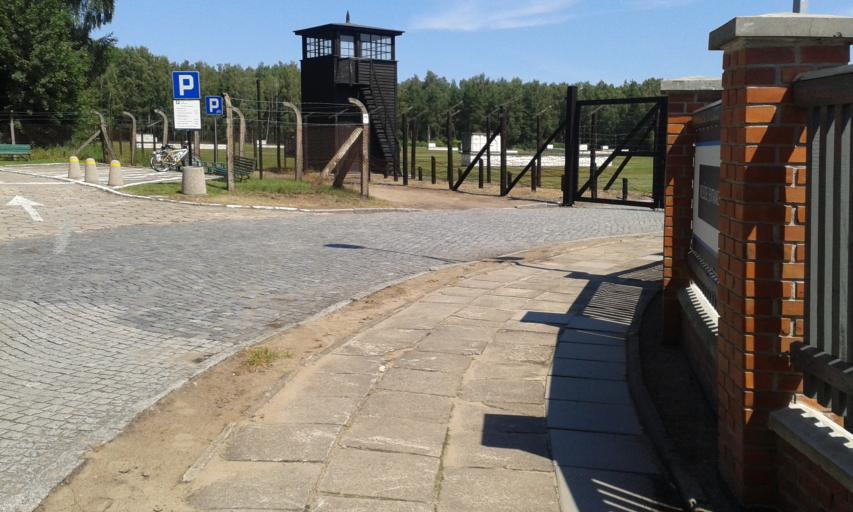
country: PL
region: Pomeranian Voivodeship
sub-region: Powiat nowodworski
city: Sztutowo
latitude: 54.3288
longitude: 19.1542
